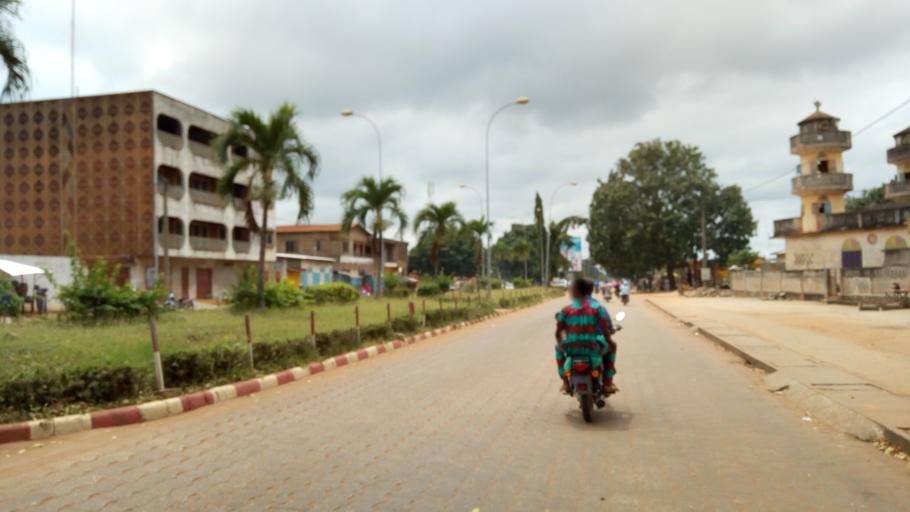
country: BJ
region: Queme
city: Porto-Novo
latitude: 6.4799
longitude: 2.6330
